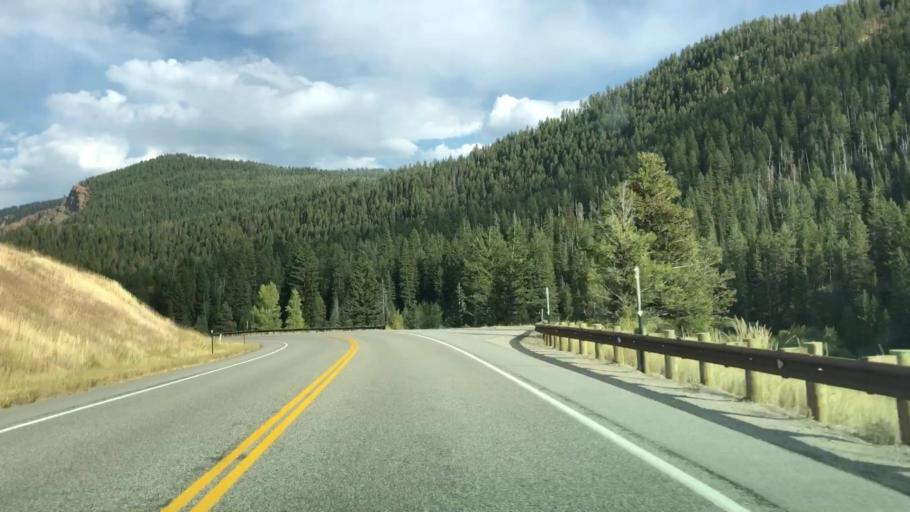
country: US
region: Wyoming
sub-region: Teton County
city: Hoback
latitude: 43.2810
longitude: -110.6074
